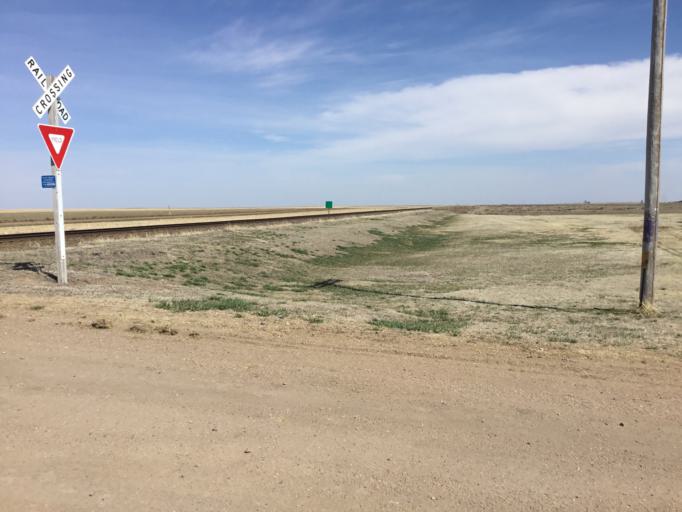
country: US
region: Kansas
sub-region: Trego County
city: WaKeeney
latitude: 39.0493
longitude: -100.0198
